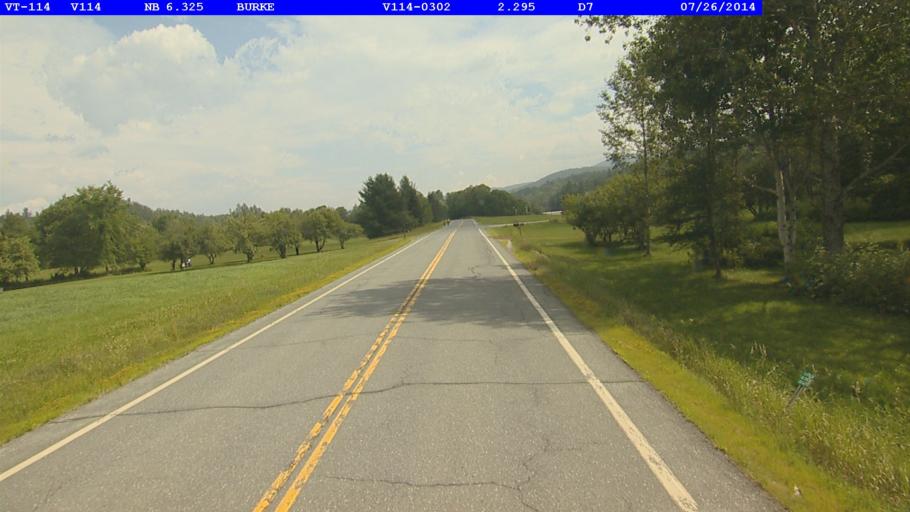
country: US
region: Vermont
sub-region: Caledonia County
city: Lyndonville
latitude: 44.6063
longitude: -71.9200
